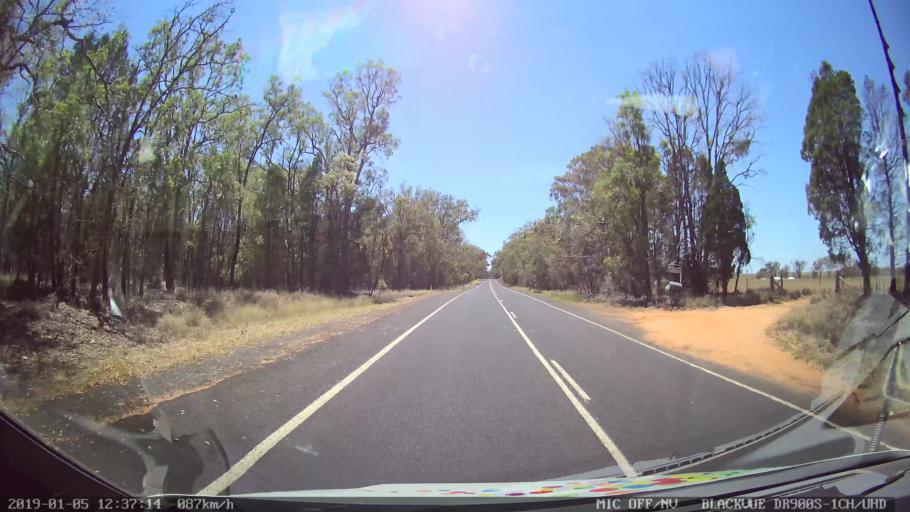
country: AU
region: New South Wales
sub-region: Warrumbungle Shire
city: Coonabarabran
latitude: -31.2042
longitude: 149.4519
